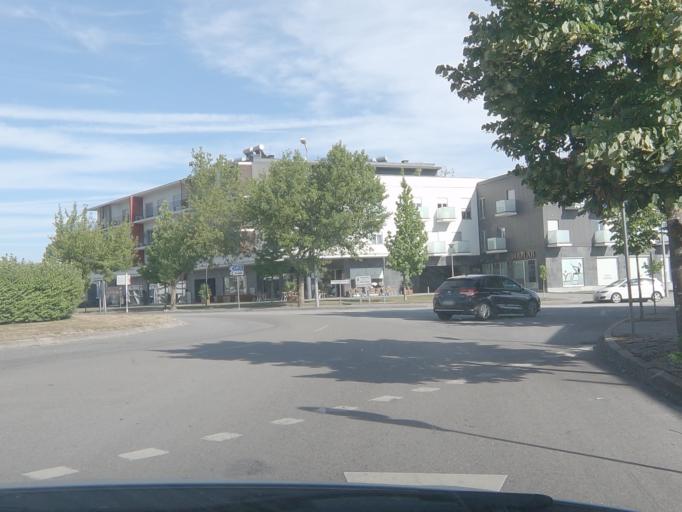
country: PT
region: Viseu
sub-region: Viseu
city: Viseu
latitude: 40.6413
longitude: -7.9183
